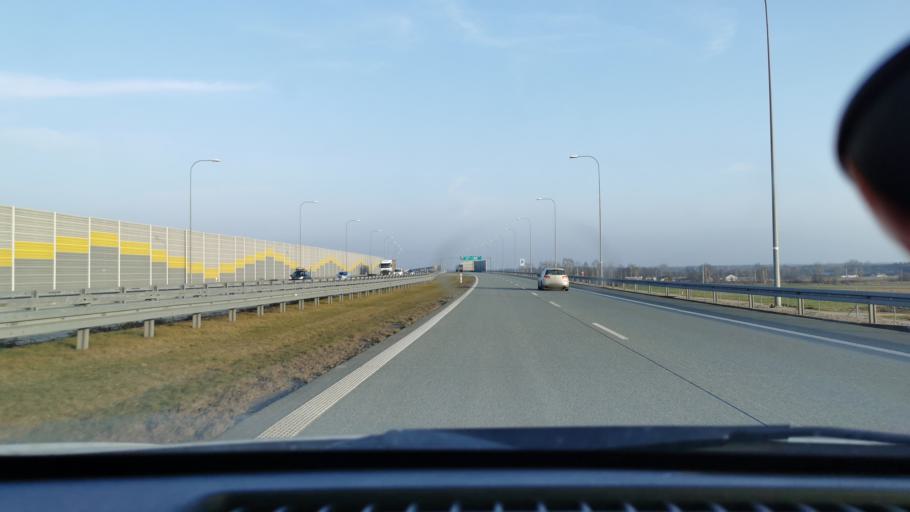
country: PL
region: Lodz Voivodeship
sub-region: Powiat laski
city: Sedziejowice
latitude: 51.5592
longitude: 19.0143
